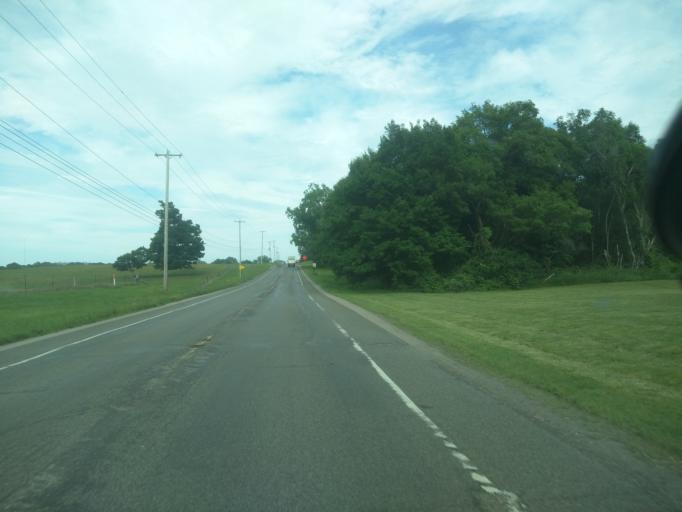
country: US
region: Michigan
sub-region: Ingham County
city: East Lansing
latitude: 42.6828
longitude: -84.4706
